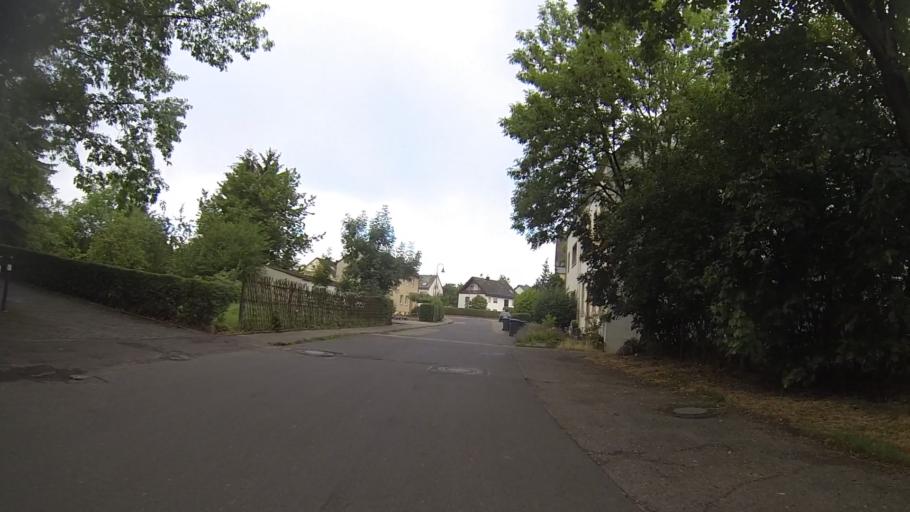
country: DE
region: Rheinland-Pfalz
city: Kenn
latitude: 49.7828
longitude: 6.6949
